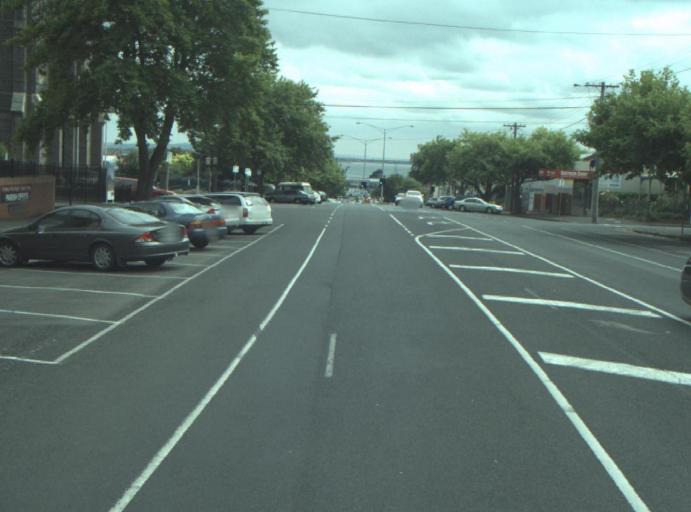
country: AU
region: Victoria
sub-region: Greater Geelong
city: Geelong
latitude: -38.1536
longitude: 144.3606
